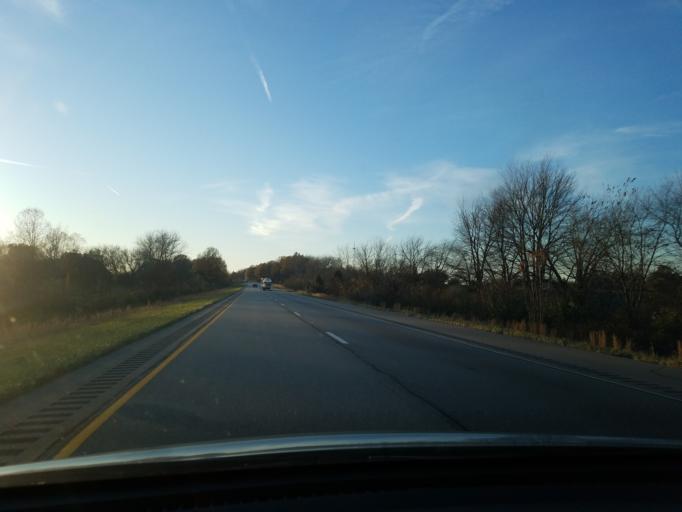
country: US
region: Indiana
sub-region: Warrick County
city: Chandler
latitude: 38.1844
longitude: -87.3805
